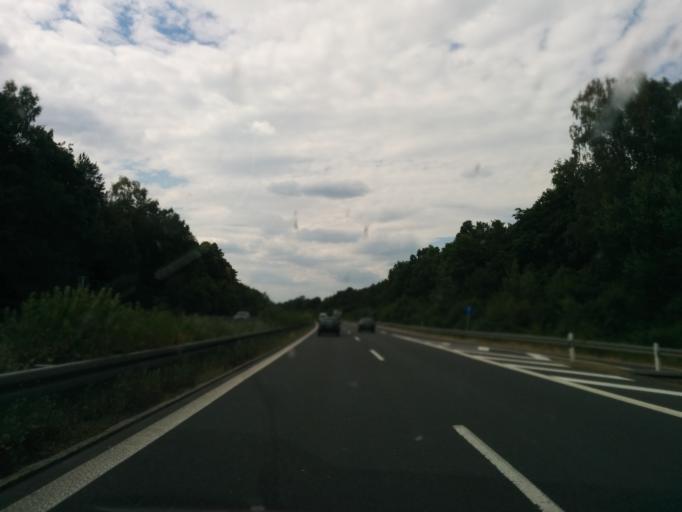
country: DE
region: Bavaria
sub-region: Upper Franconia
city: Gundelsheim
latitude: 49.9442
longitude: 10.9043
